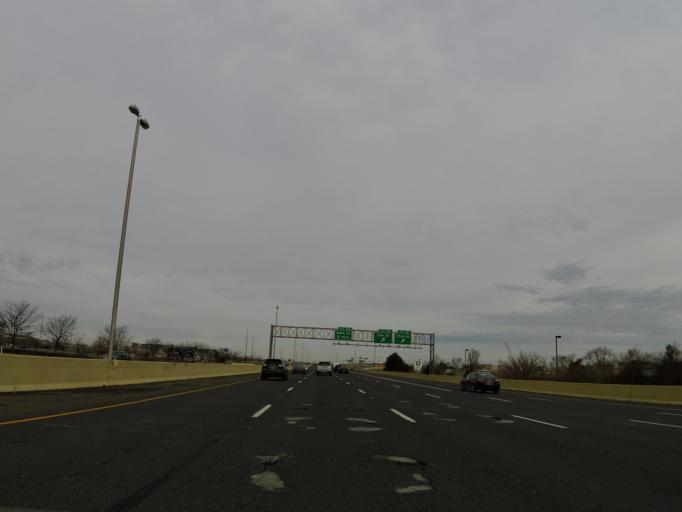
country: US
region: Indiana
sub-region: Marion County
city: Speedway
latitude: 39.8747
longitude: -86.2687
